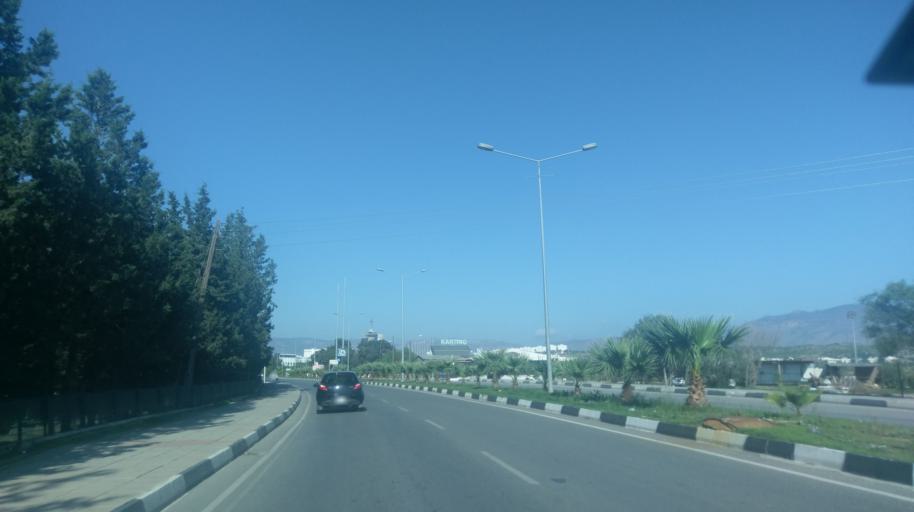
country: CY
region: Lefkosia
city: Nicosia
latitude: 35.2189
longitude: 33.3309
